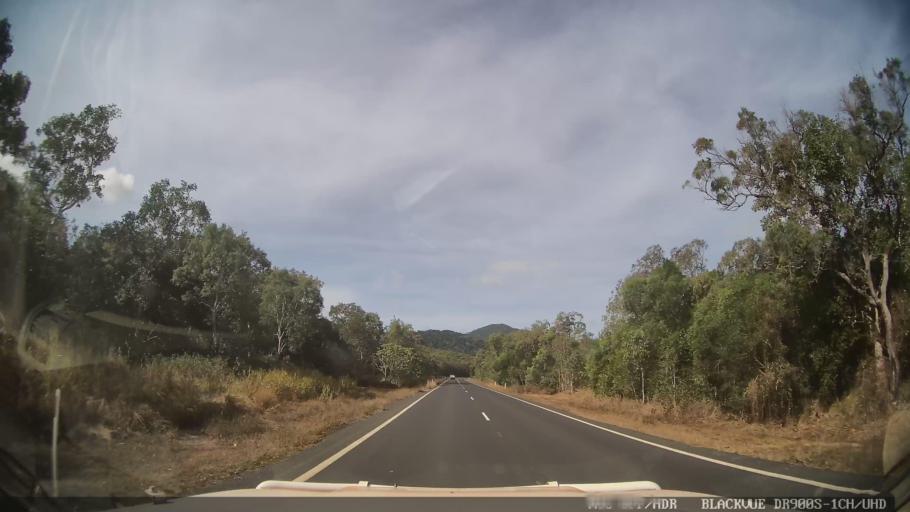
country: AU
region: Queensland
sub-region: Cook
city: Cooktown
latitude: -15.5034
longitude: 145.2363
